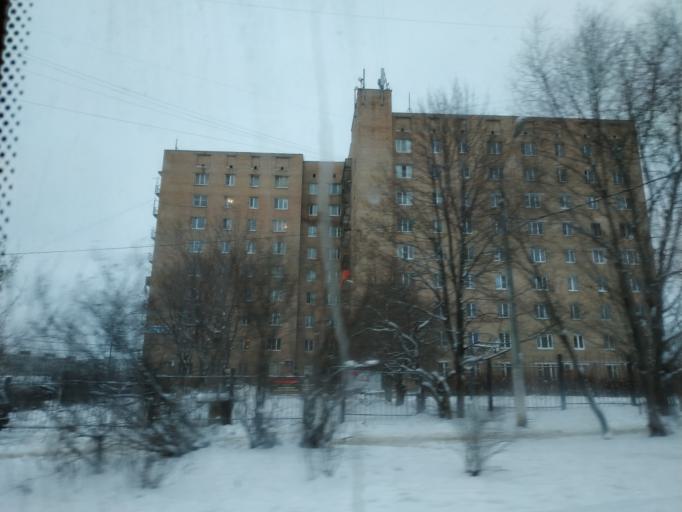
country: RU
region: Moskovskaya
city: Shchelkovo
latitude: 55.9319
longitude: 37.9902
